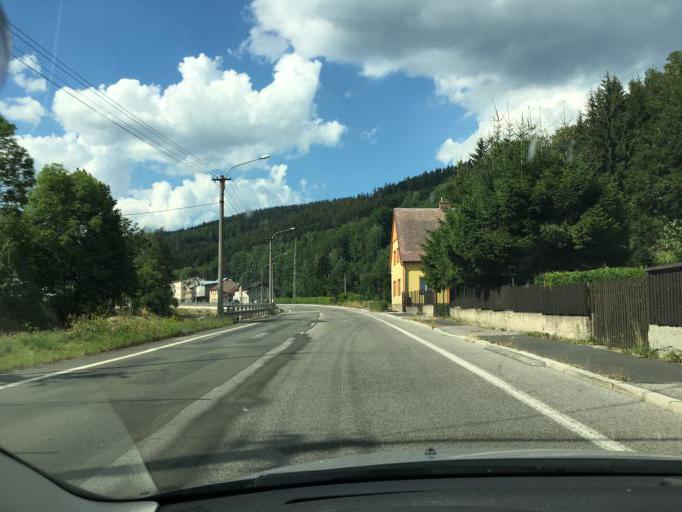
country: CZ
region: Kralovehradecky
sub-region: Okres Trutnov
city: Vrchlabi
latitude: 50.6503
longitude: 15.6052
